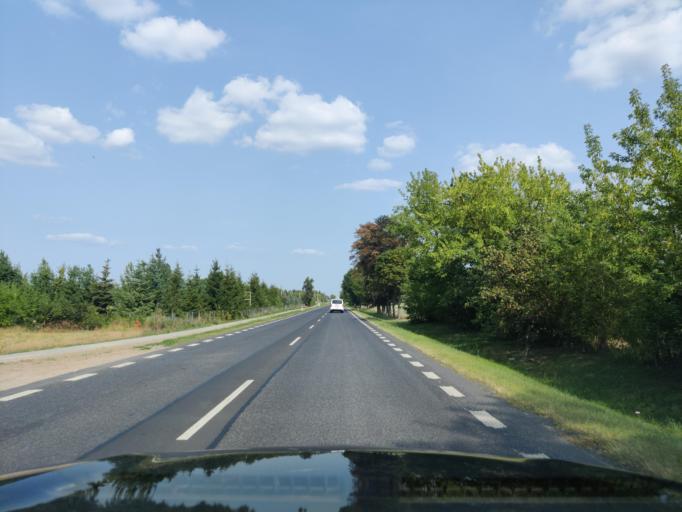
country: PL
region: Masovian Voivodeship
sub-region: Powiat makowski
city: Rozan
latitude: 52.8804
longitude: 21.3714
